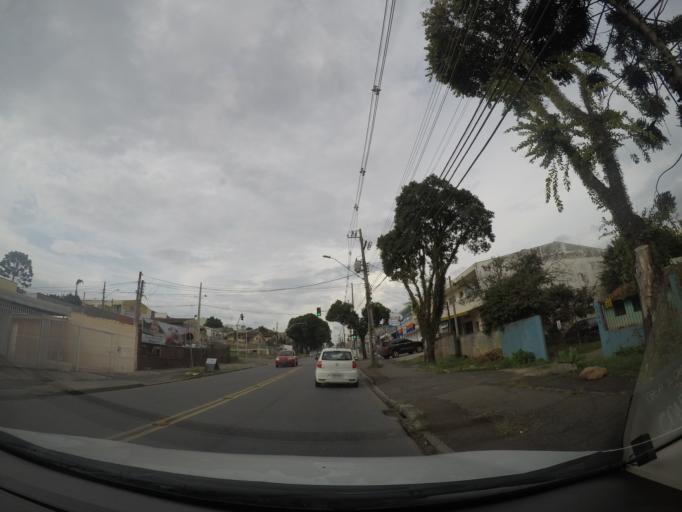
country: BR
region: Parana
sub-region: Sao Jose Dos Pinhais
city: Sao Jose dos Pinhais
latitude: -25.5141
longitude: -49.2671
